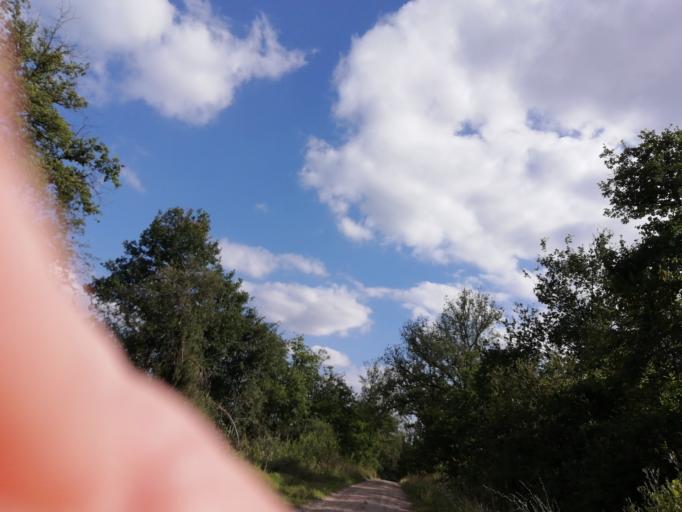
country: FR
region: Poitou-Charentes
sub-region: Departement de la Vienne
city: Thure
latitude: 46.8478
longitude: 0.4561
